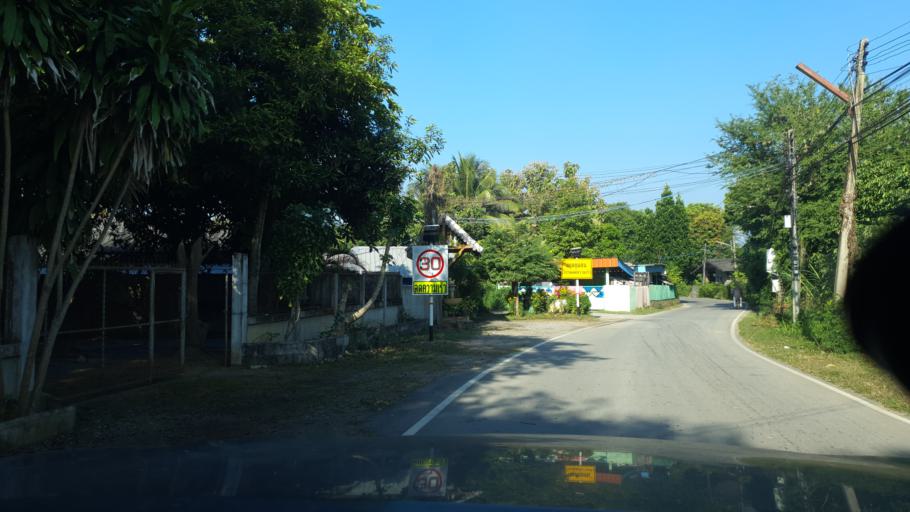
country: TH
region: Chiang Mai
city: San Kamphaeng
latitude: 18.7513
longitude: 99.1659
